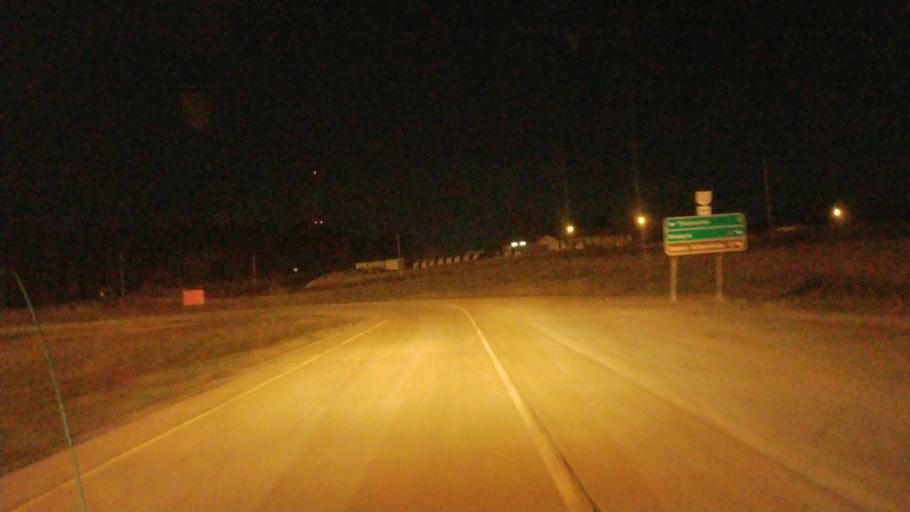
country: US
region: Ohio
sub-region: Licking County
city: Harbor Hills
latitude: 39.9448
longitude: -82.4069
